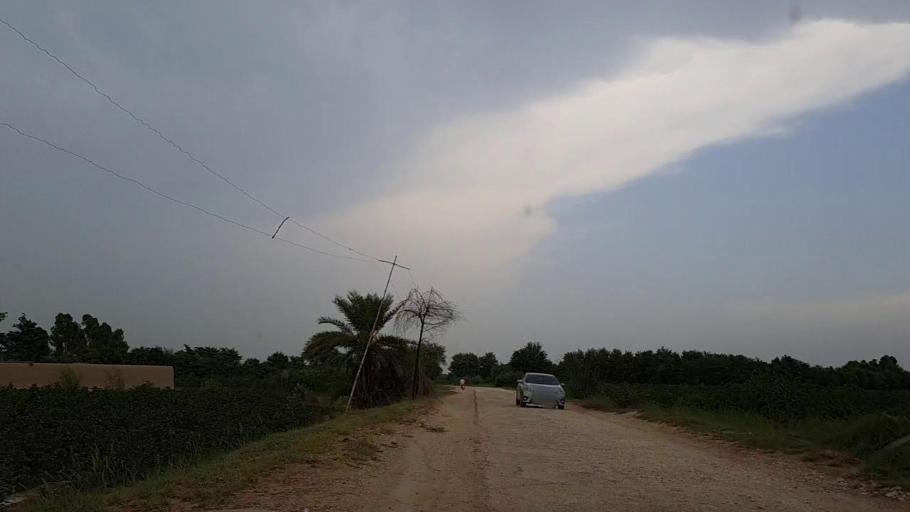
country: PK
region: Sindh
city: Mirpur Mathelo
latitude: 27.8410
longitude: 69.6210
